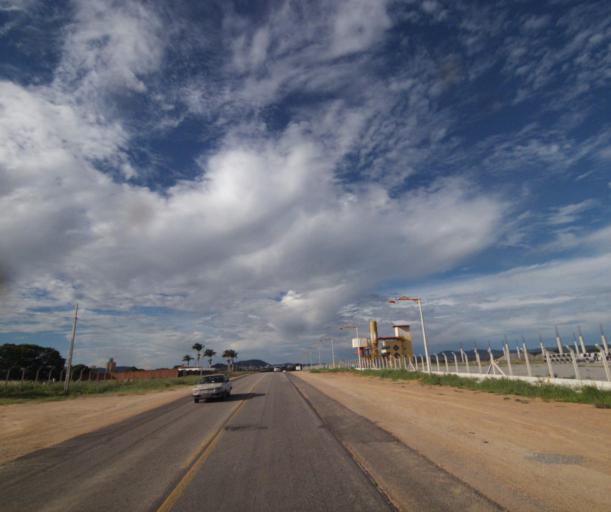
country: BR
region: Bahia
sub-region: Guanambi
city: Guanambi
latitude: -14.2577
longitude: -42.7822
